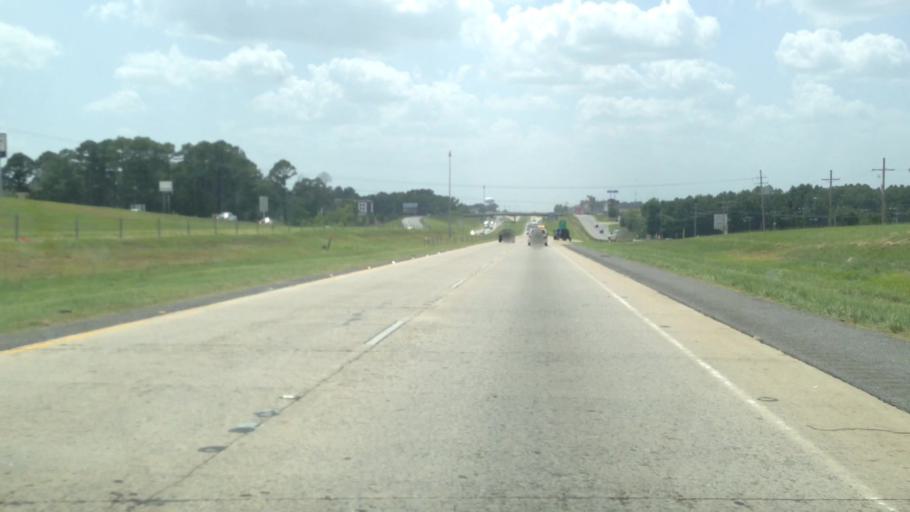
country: US
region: Louisiana
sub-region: Lincoln Parish
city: Ruston
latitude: 32.5405
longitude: -92.6172
